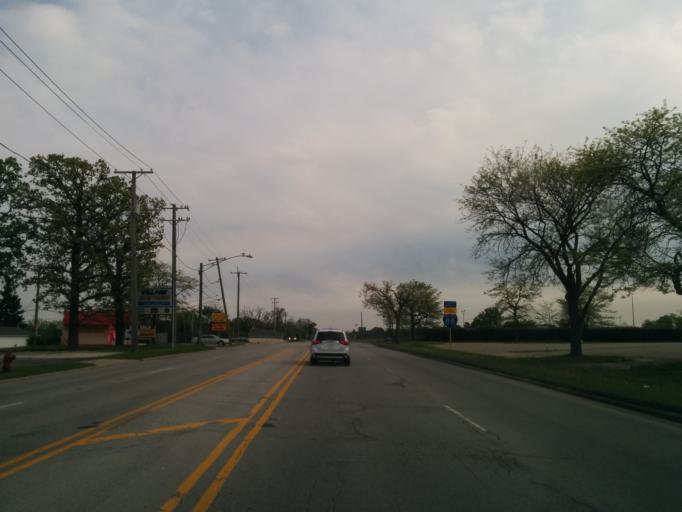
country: US
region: Illinois
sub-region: Kane County
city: North Aurora
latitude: 41.7974
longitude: -88.3243
